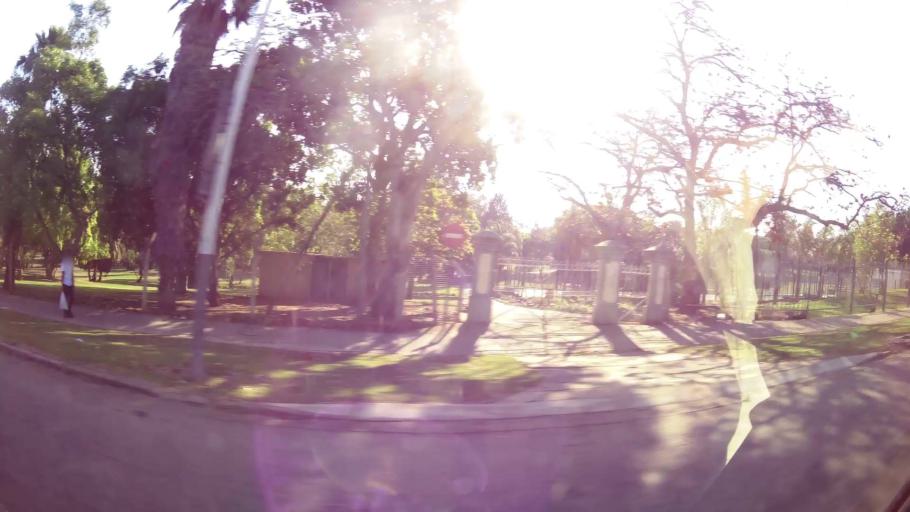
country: ZA
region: Eastern Cape
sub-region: Nelson Mandela Bay Metropolitan Municipality
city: Uitenhage
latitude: -33.7633
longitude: 25.4023
